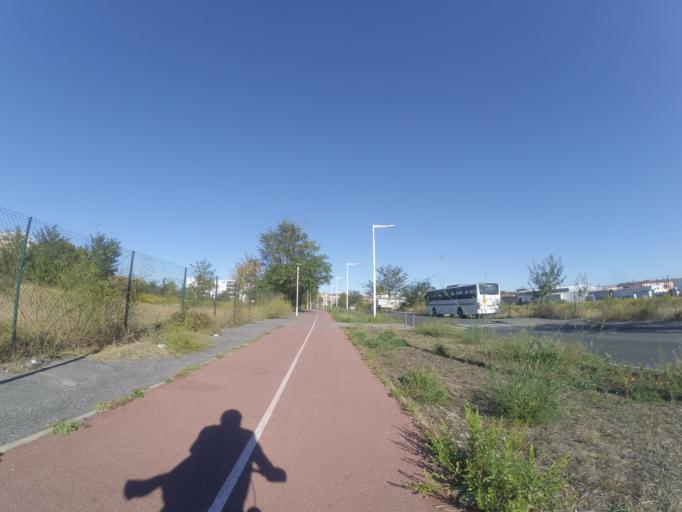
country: FR
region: Languedoc-Roussillon
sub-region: Departement des Pyrenees-Orientales
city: Perpignan
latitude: 42.6917
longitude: 2.8776
